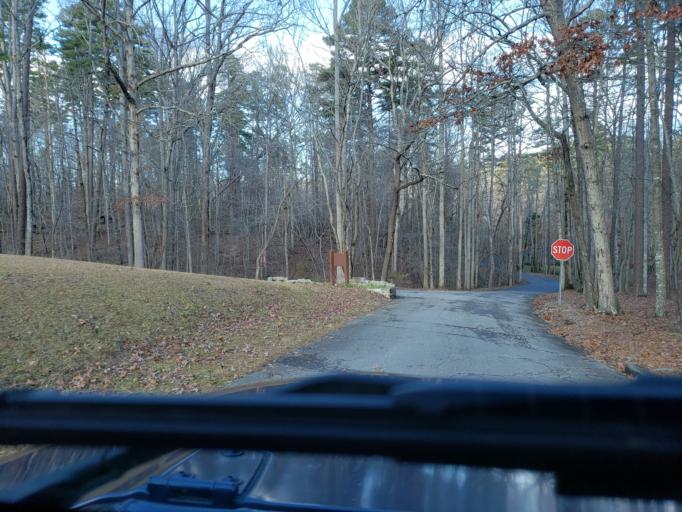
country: US
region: North Carolina
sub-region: Cleveland County
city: Kings Mountain
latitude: 35.1494
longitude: -81.3452
